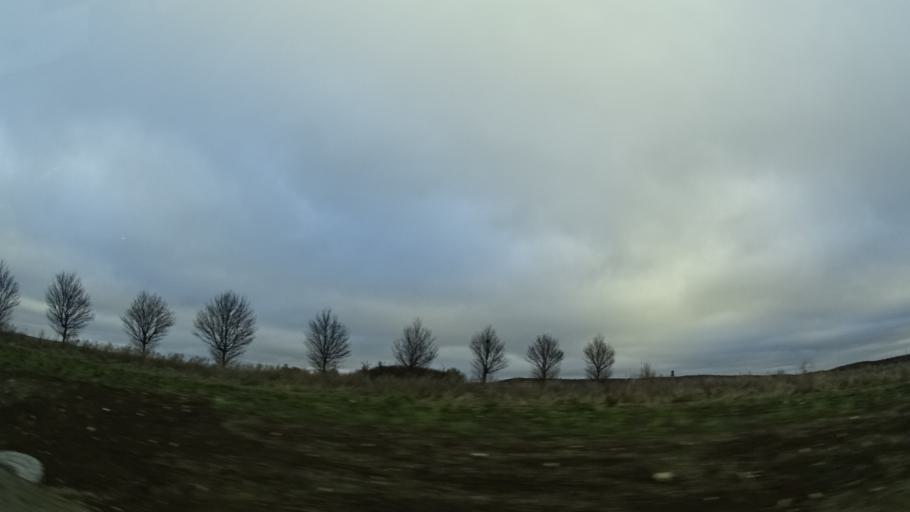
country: DE
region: Thuringia
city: Rottenbach
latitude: 50.7400
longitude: 11.1575
